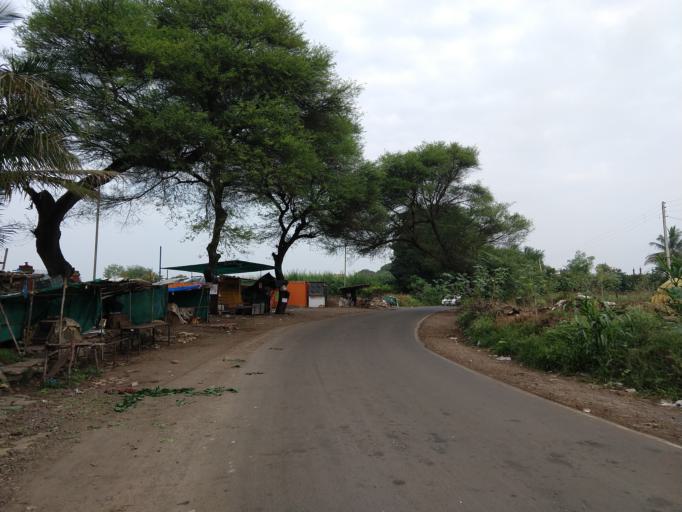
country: IN
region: Maharashtra
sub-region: Pune Division
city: Sasvad
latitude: 18.3602
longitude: 73.9956
